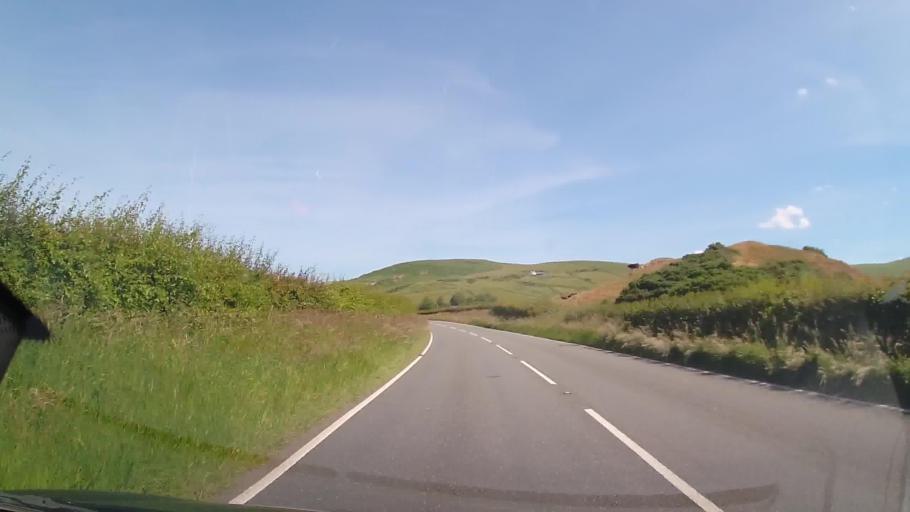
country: GB
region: Wales
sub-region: Gwynedd
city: Tywyn
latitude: 52.5696
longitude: -4.0702
